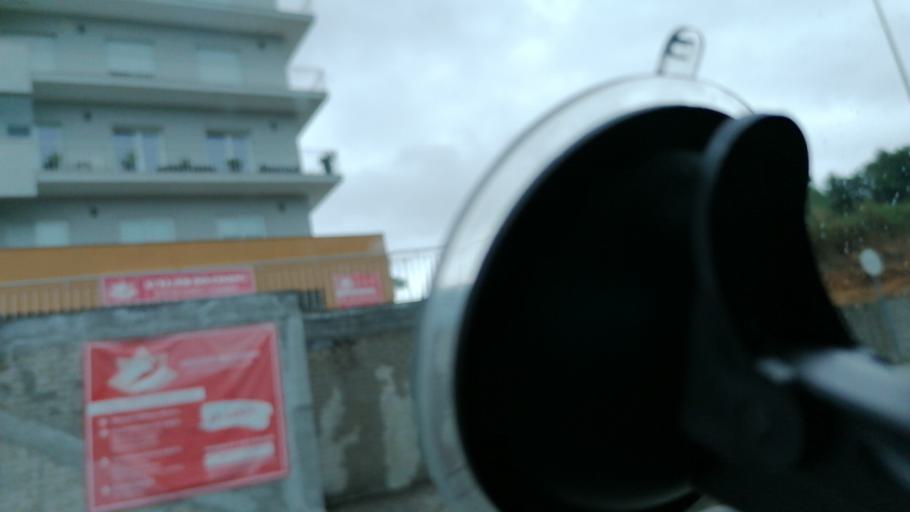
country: PT
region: Porto
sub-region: Penafiel
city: Penafiel
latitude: 41.2114
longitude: -8.2844
